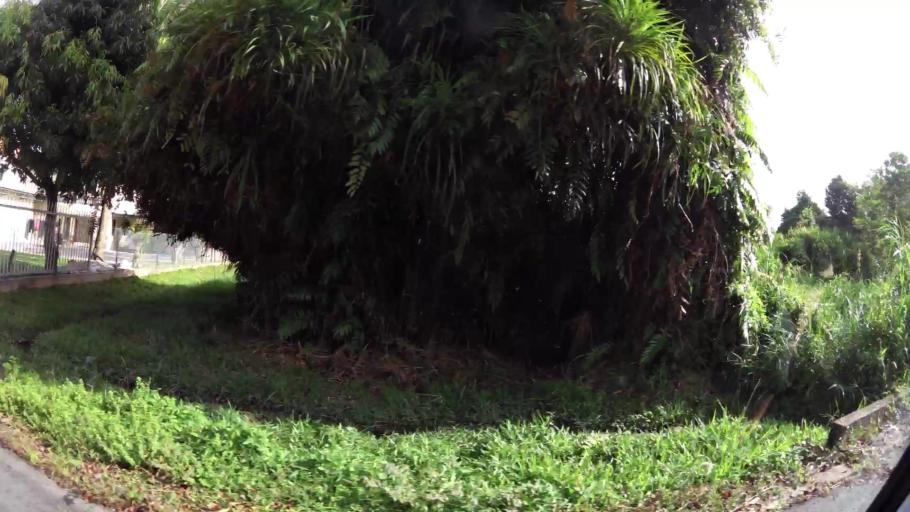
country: BN
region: Brunei and Muara
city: Bandar Seri Begawan
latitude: 4.9070
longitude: 114.8922
